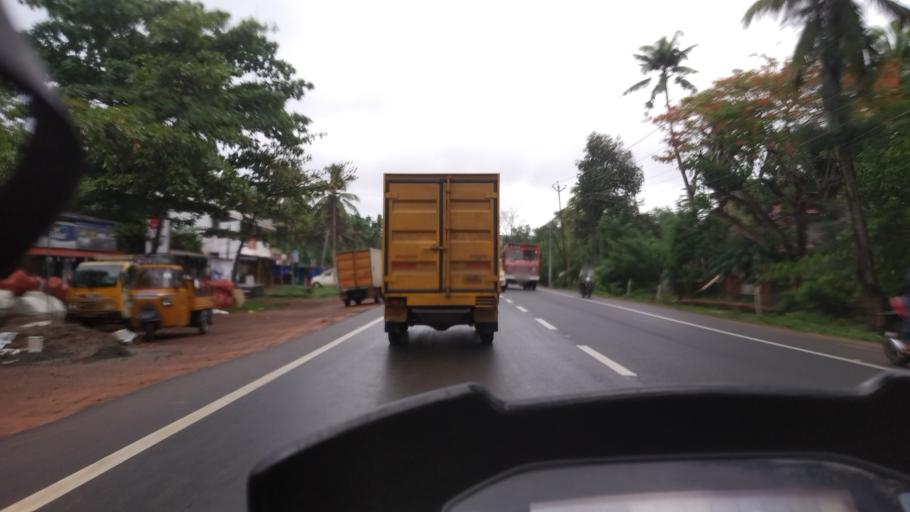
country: IN
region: Kerala
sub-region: Alappuzha
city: Mavelikara
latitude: 9.3162
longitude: 76.4276
